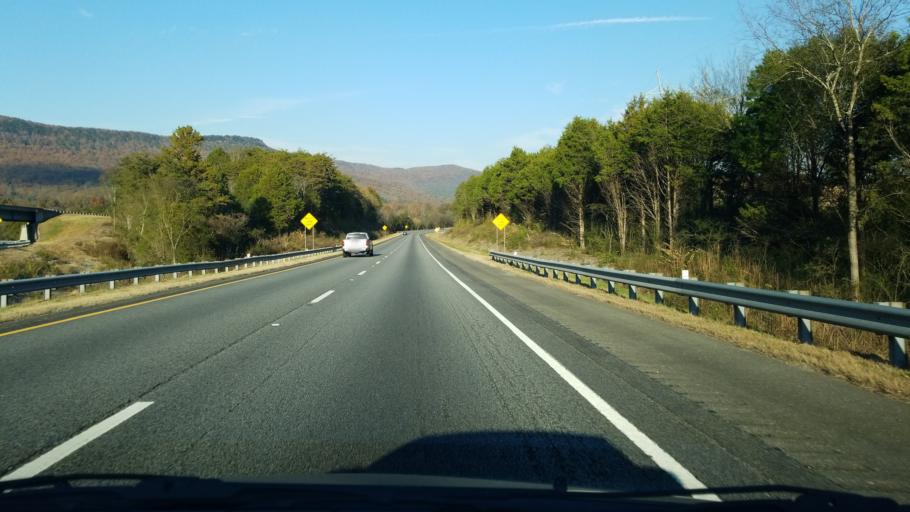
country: US
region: Georgia
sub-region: Walker County
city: Lookout Mountain
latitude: 34.9667
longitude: -85.4516
